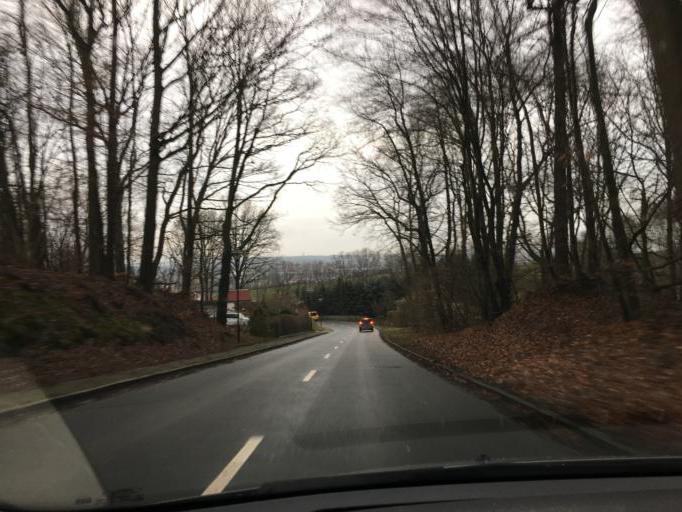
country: DE
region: Saxony
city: Pfaffroda
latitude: 50.8500
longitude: 12.5332
